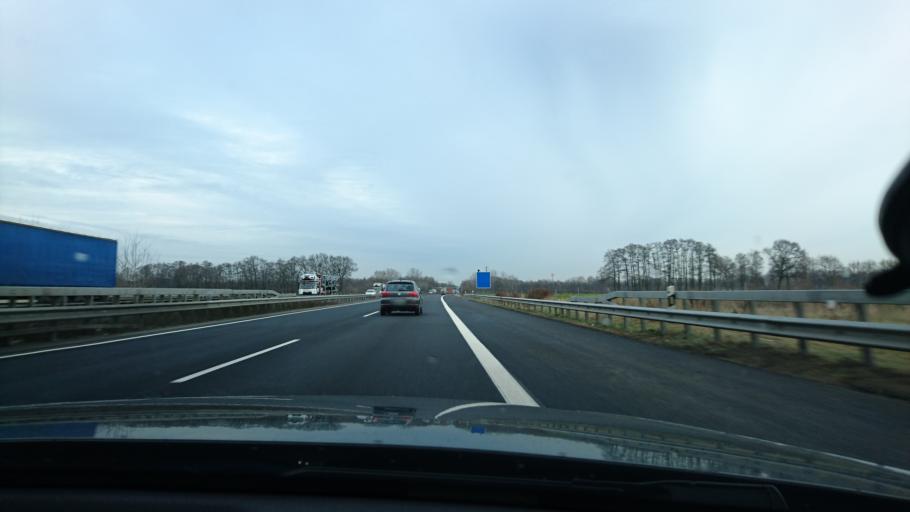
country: DE
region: Lower Saxony
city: Holdorf
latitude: 52.5881
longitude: 8.1107
